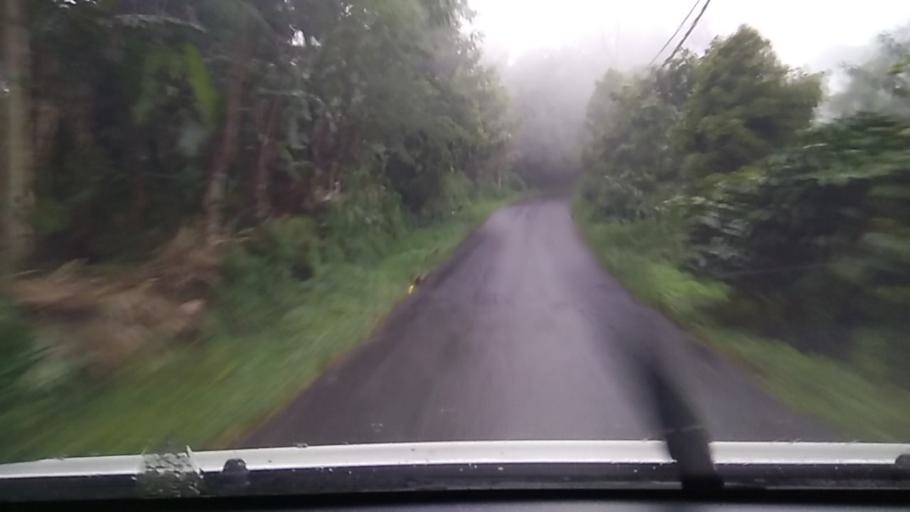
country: ID
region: Bali
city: Banjar Ambengan
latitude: -8.2012
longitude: 115.1760
